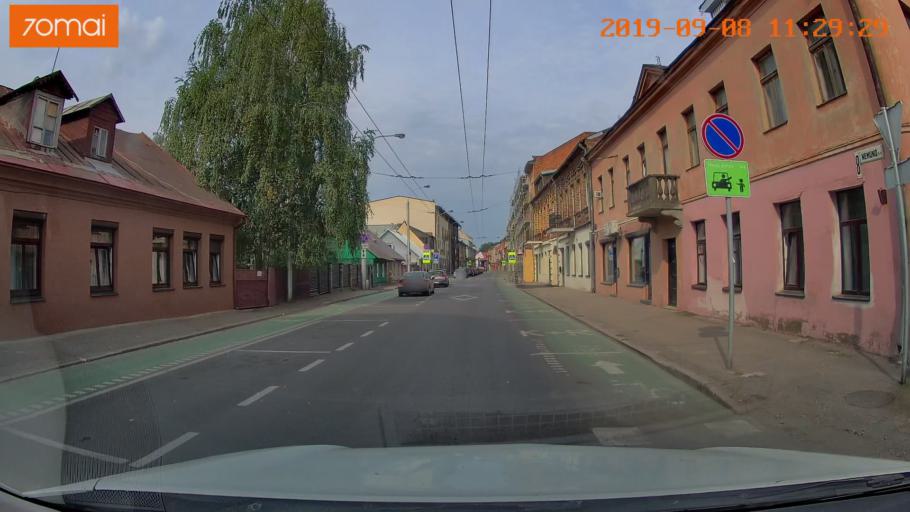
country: LT
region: Kauno apskritis
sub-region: Kaunas
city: Kaunas
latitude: 54.8950
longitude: 23.9014
